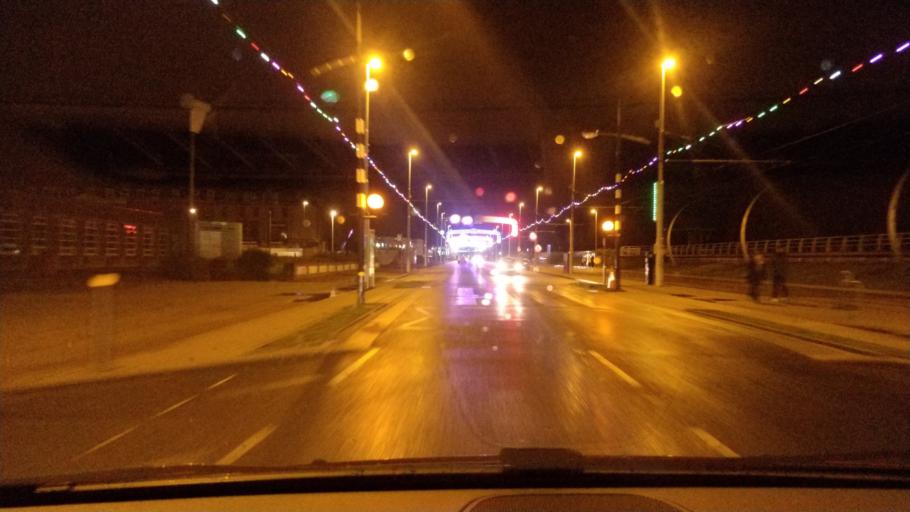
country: GB
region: England
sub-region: Blackpool
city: Blackpool
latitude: 53.7836
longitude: -3.0580
